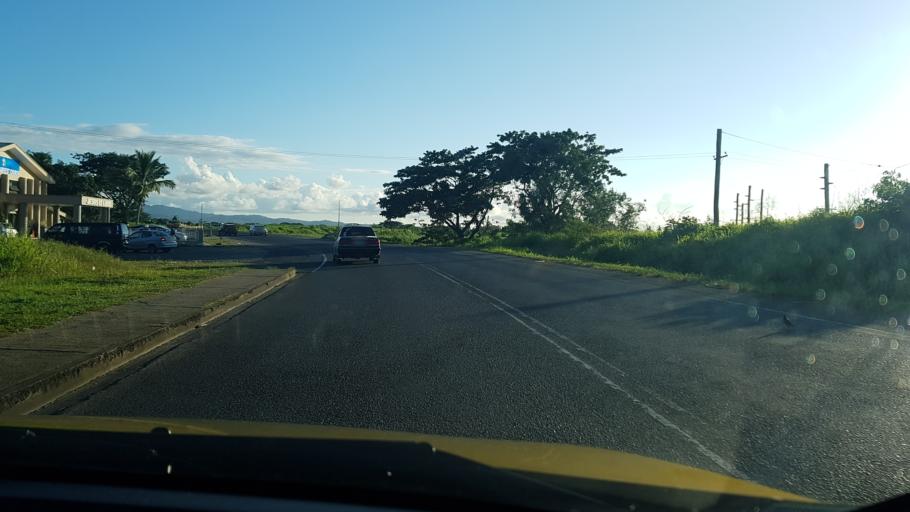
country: FJ
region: Western
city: Nadi
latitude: -17.7650
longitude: 177.4549
